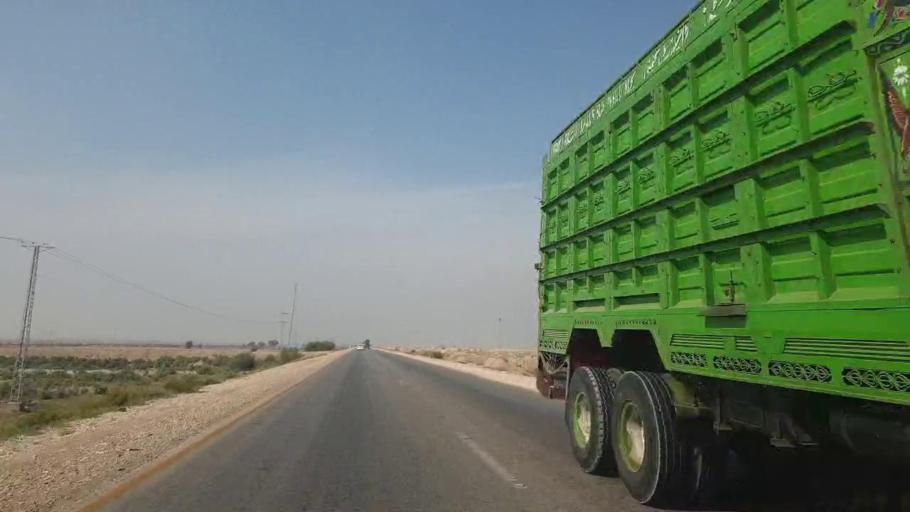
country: PK
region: Sindh
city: Sann
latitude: 25.9182
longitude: 68.2196
